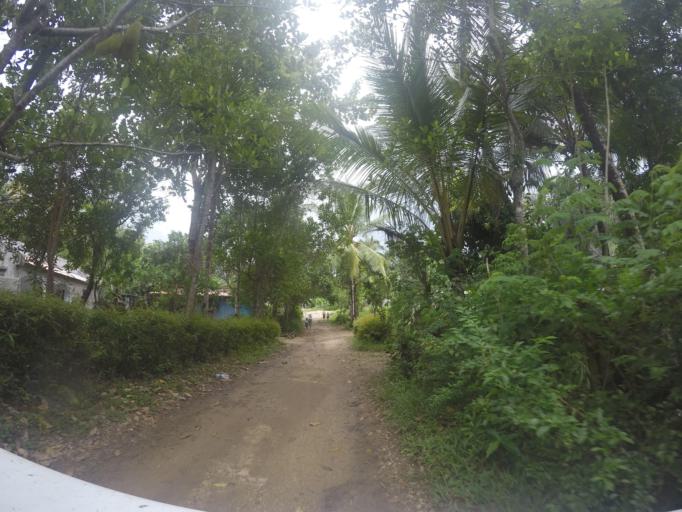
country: TL
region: Lautem
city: Lospalos
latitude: -8.5239
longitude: 126.9926
